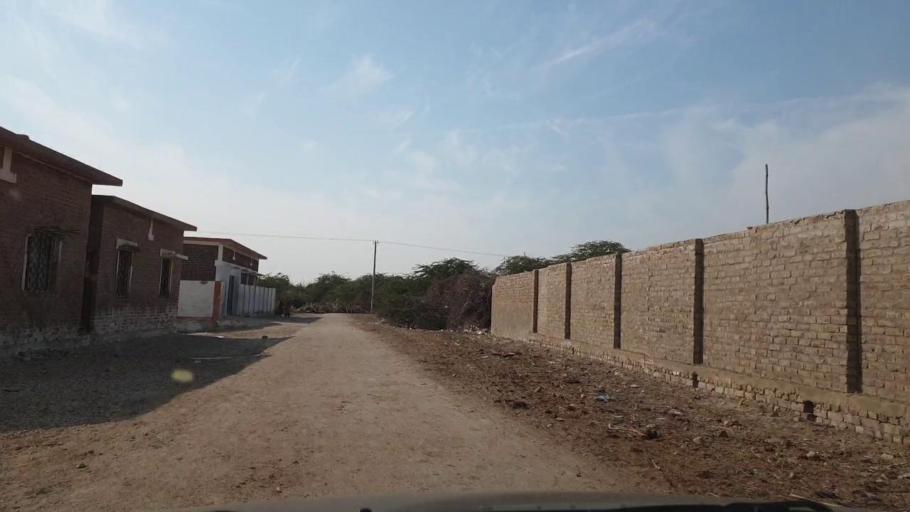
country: PK
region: Sindh
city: Khadro
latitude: 26.1250
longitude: 68.7191
